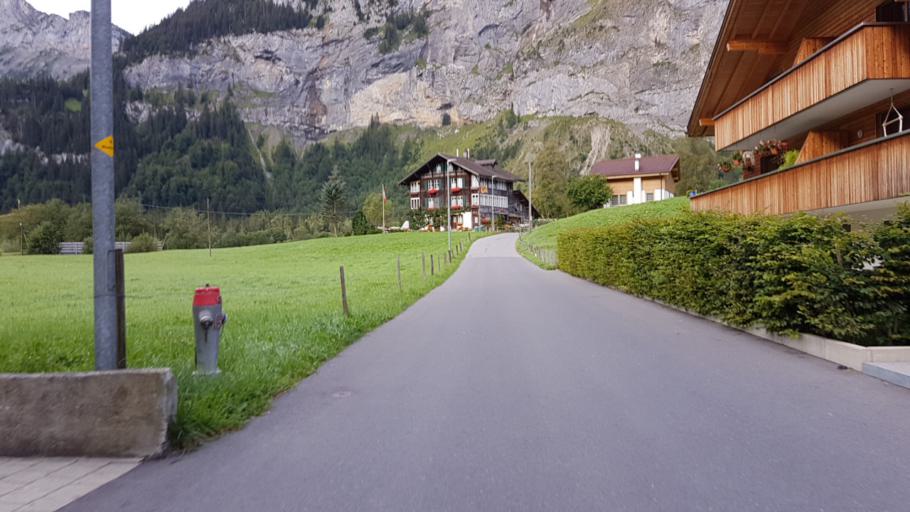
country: CH
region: Bern
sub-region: Frutigen-Niedersimmental District
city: Kandersteg
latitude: 46.4910
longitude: 7.6676
